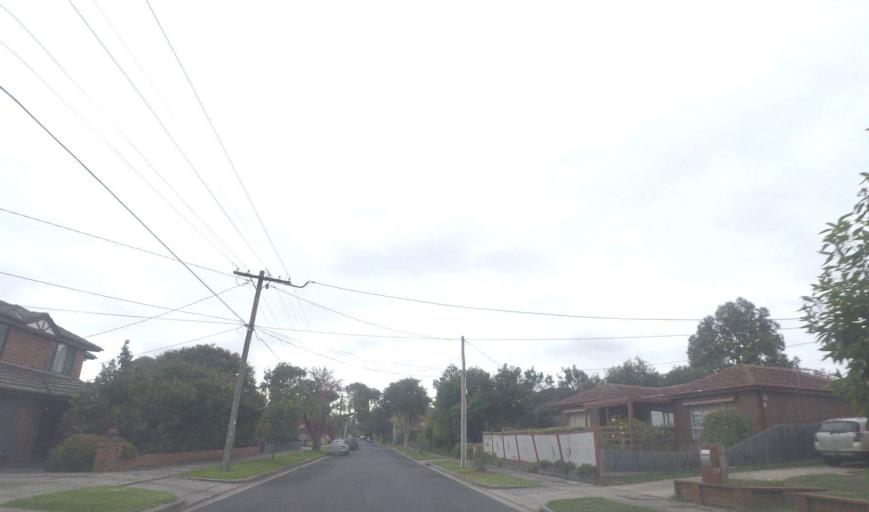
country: AU
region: Victoria
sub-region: Whitehorse
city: Blackburn North
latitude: -37.8062
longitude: 145.1638
